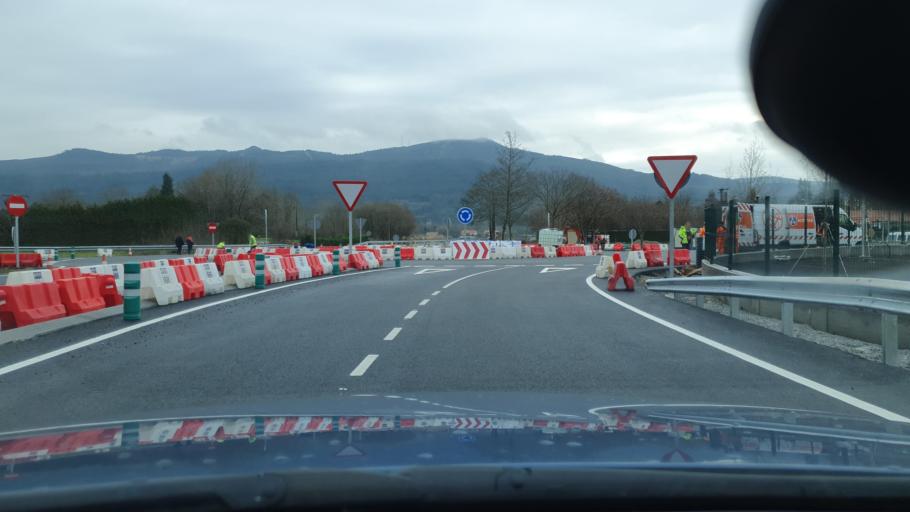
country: ES
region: Galicia
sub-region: Provincia da Coruna
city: Padron
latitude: 42.7574
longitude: -8.6708
